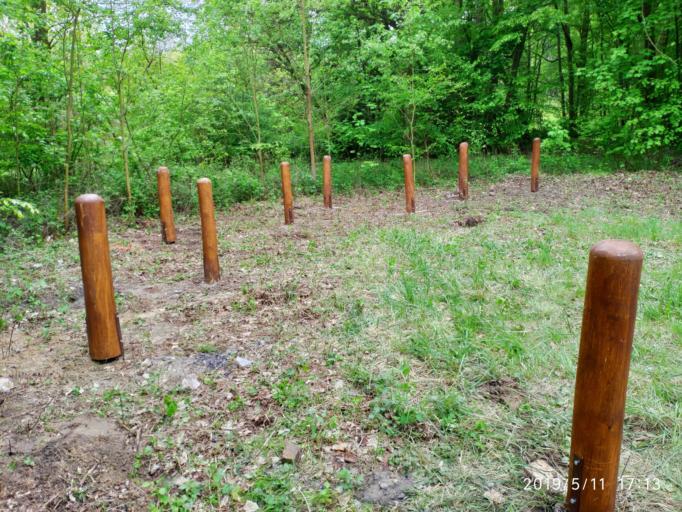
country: PL
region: Lubusz
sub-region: Powiat zielonogorski
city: Sulechow
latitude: 52.0242
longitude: 15.5556
